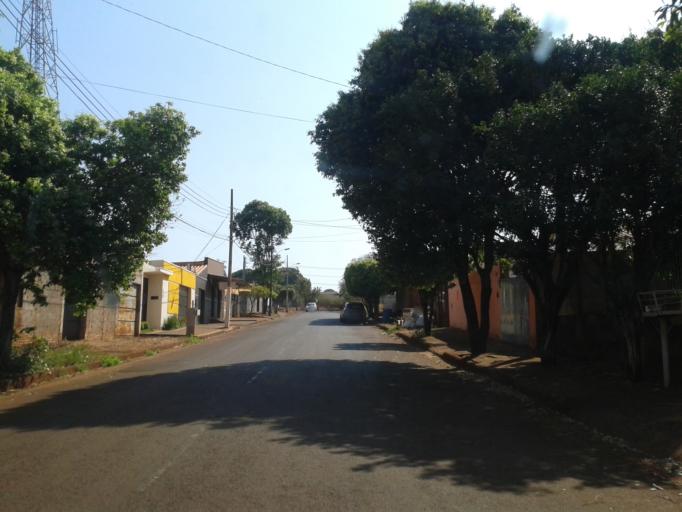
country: BR
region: Minas Gerais
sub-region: Ituiutaba
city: Ituiutaba
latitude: -18.9624
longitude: -49.4796
